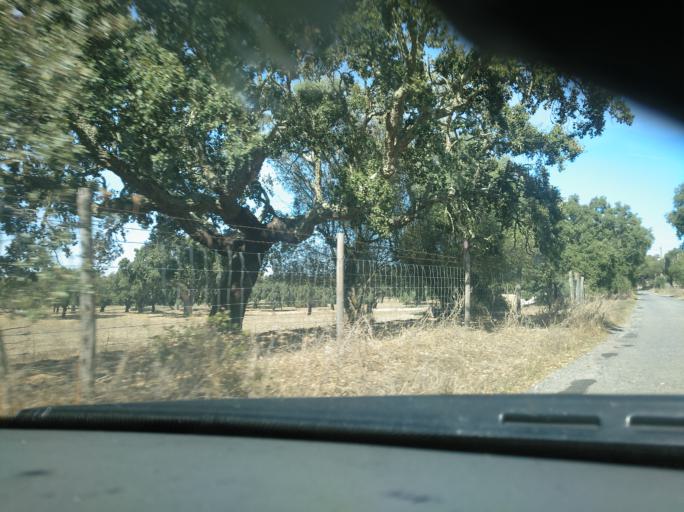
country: PT
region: Evora
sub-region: Arraiolos
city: Arraiolos
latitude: 38.6955
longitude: -8.0933
